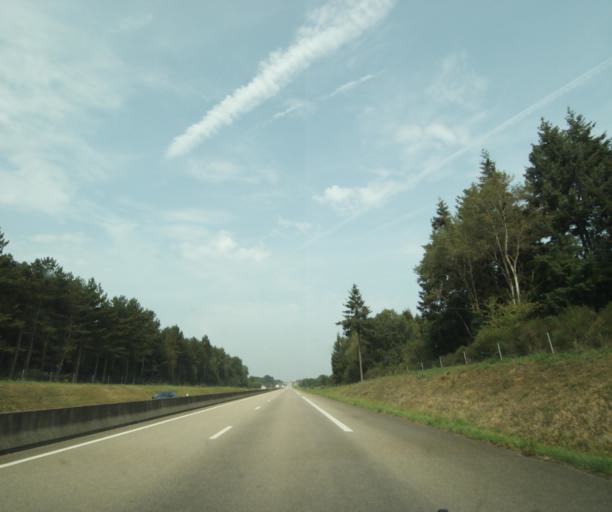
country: FR
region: Lower Normandy
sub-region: Departement du Calvados
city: Falaise
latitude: 48.8343
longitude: -0.1512
